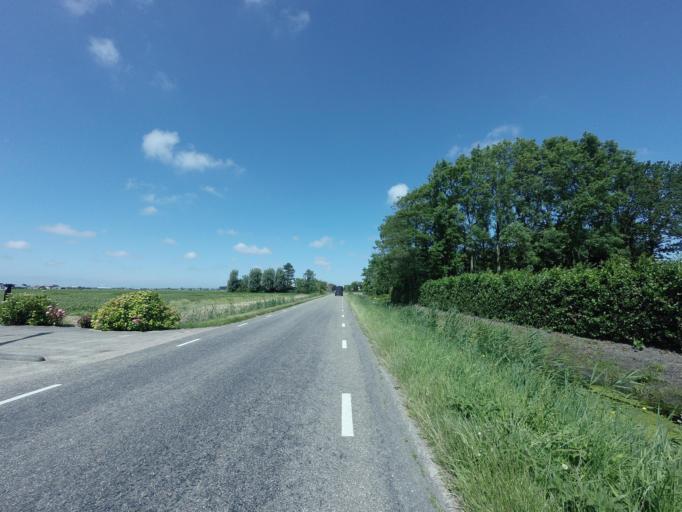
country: NL
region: North Holland
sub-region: Gemeente Schagen
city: Schagen
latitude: 52.8838
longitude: 4.8329
